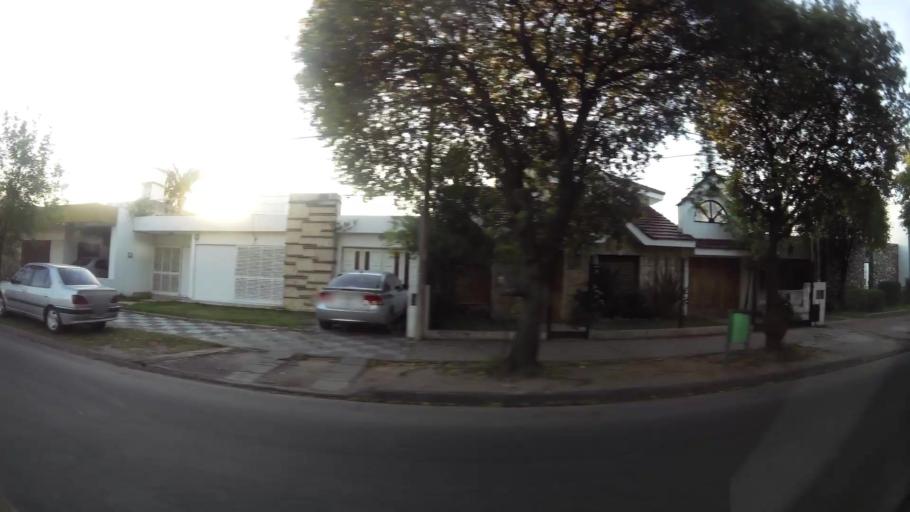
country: AR
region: Cordoba
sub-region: Departamento de Capital
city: Cordoba
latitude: -31.3734
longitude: -64.2222
